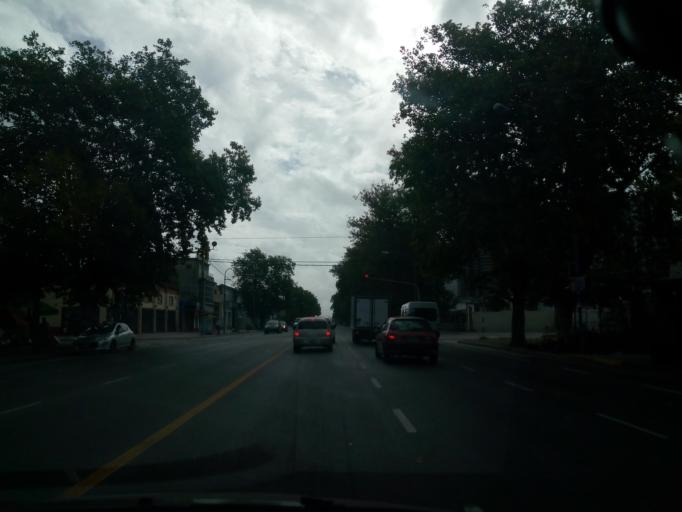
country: AR
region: Buenos Aires
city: Mar del Plata
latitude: -37.9845
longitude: -57.5741
